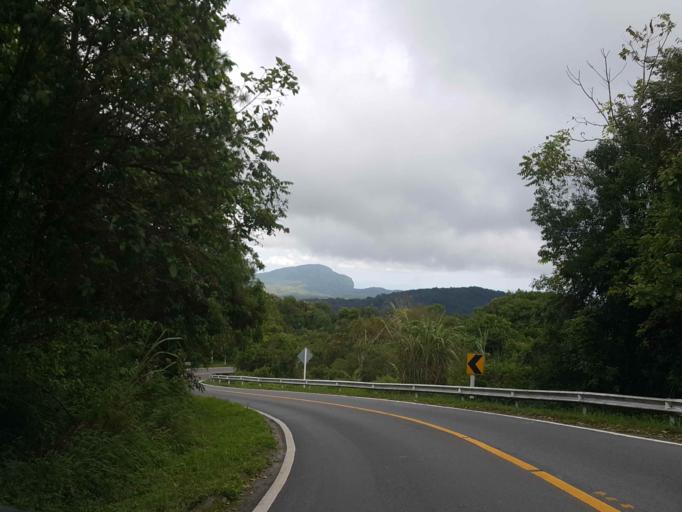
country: TH
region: Chiang Mai
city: Mae Chaem
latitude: 18.5402
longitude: 98.4889
